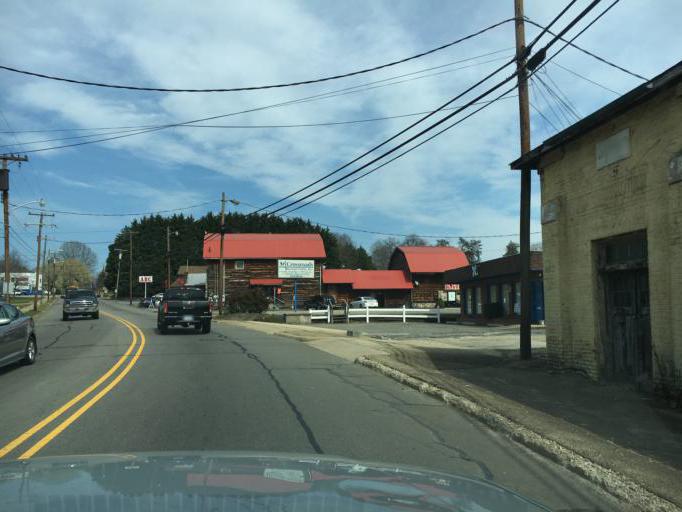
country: US
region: North Carolina
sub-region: McDowell County
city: Marion
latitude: 35.6867
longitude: -82.0023
